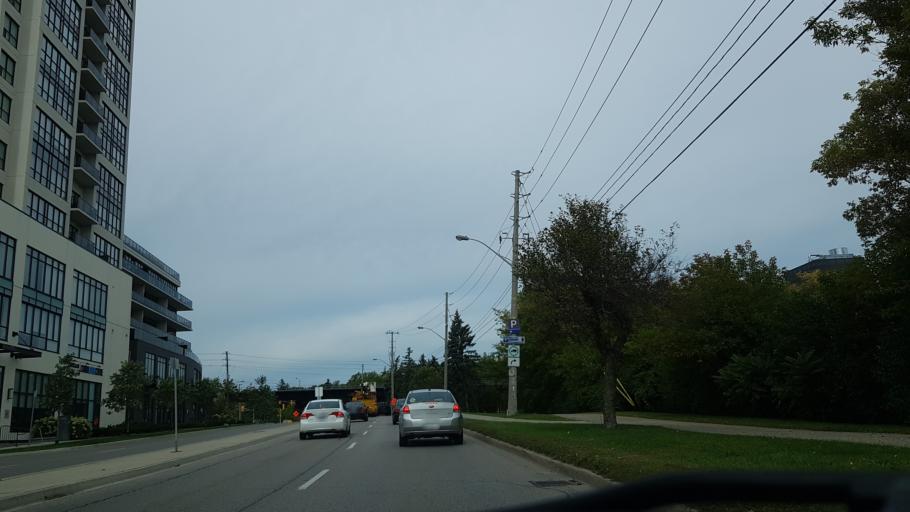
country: CA
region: Ontario
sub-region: Wellington County
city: Guelph
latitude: 43.5454
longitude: -80.2430
